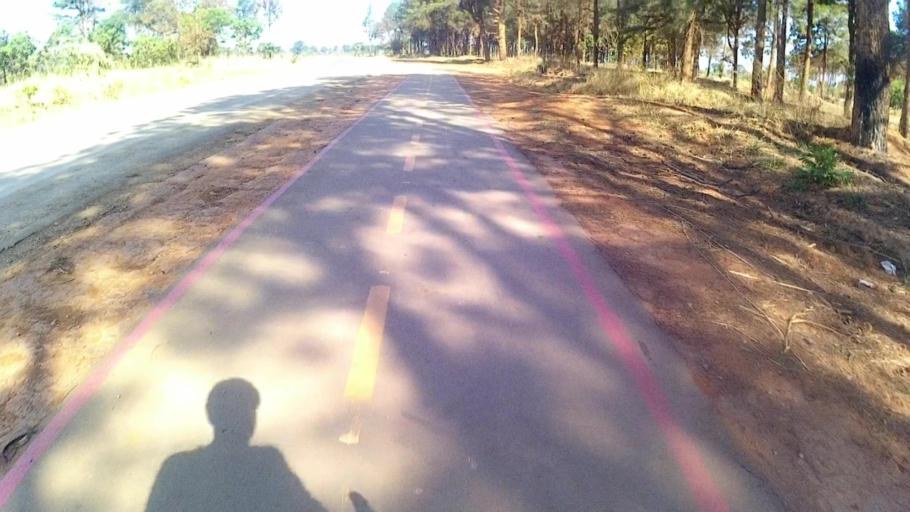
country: BR
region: Federal District
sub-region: Brasilia
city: Brasilia
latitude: -15.6795
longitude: -48.2277
